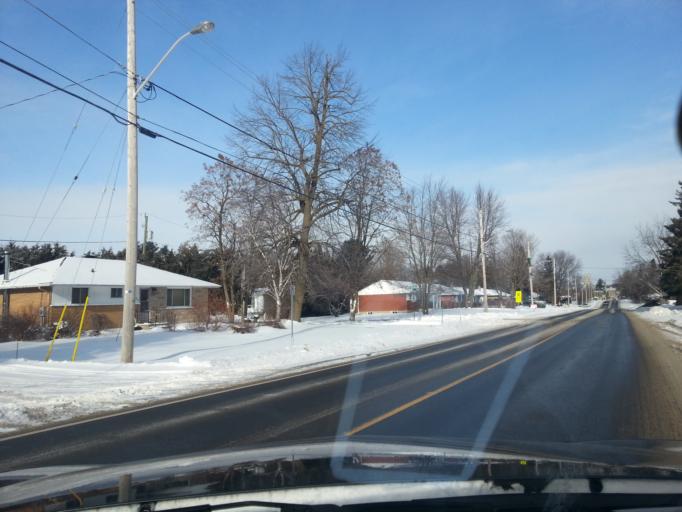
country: CA
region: Ontario
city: Carleton Place
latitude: 45.2182
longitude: -76.1966
